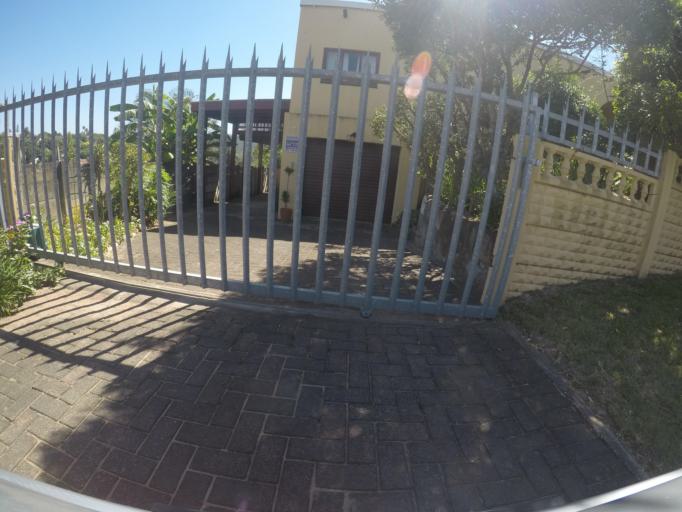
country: ZA
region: Eastern Cape
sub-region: Buffalo City Metropolitan Municipality
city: East London
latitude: -32.9737
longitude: 27.9204
